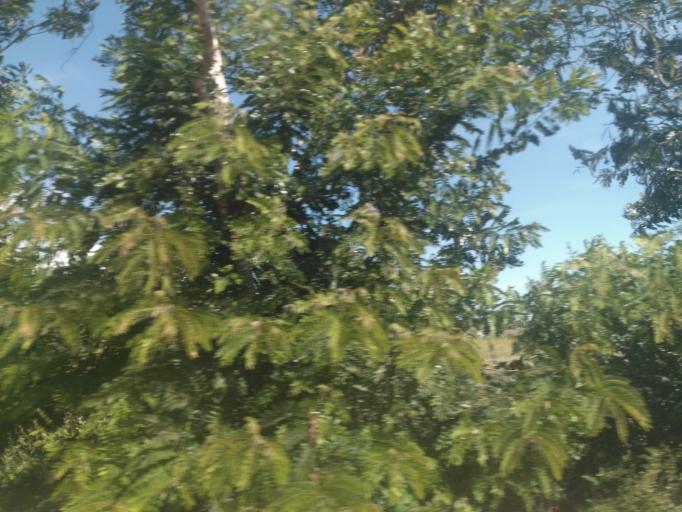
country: TZ
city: Kiwengwa
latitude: -5.9939
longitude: 39.3378
